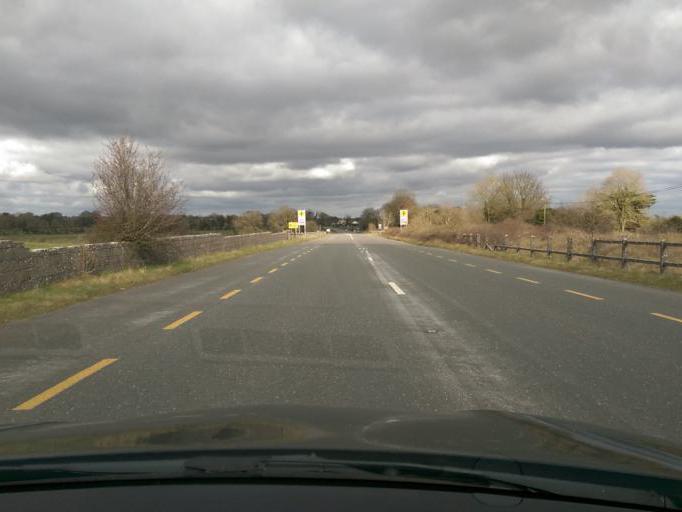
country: IE
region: Connaught
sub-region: County Galway
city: Ballinasloe
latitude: 53.3434
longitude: -8.0980
